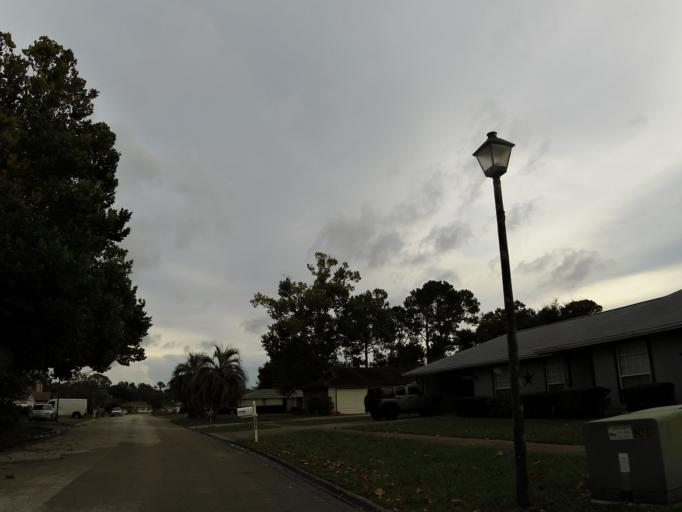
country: US
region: Florida
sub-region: Duval County
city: Neptune Beach
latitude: 30.3041
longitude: -81.5184
